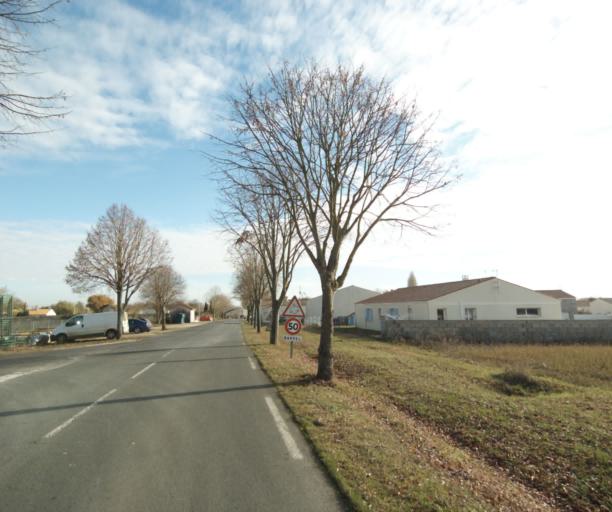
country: FR
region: Poitou-Charentes
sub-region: Departement de la Charente-Maritime
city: Corme-Royal
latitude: 45.7022
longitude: -0.7878
